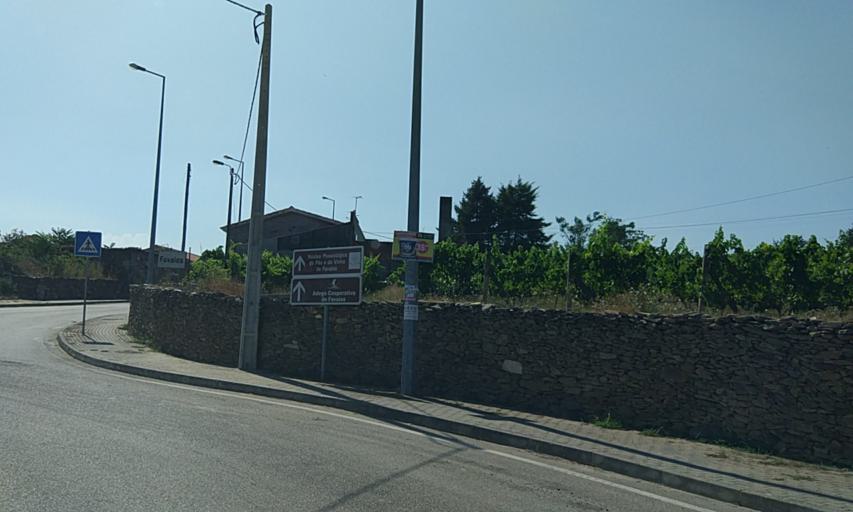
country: PT
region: Vila Real
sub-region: Sabrosa
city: Sabrosa
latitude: 41.2634
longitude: -7.4907
